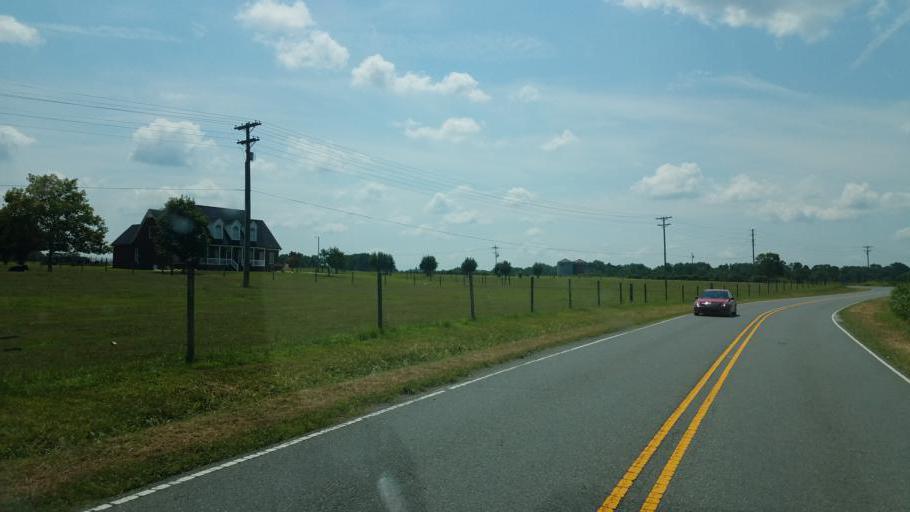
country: US
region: North Carolina
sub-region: Cleveland County
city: Kings Mountain
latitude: 35.2961
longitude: -81.3554
